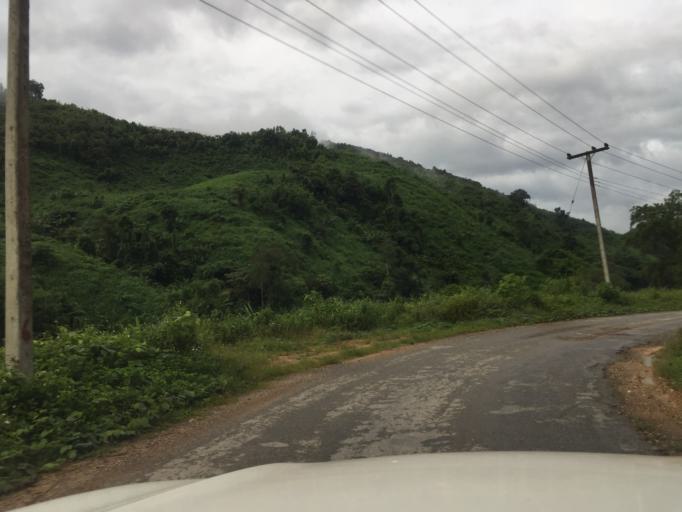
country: LA
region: Oudomxai
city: Muang La
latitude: 21.0297
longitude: 102.2367
